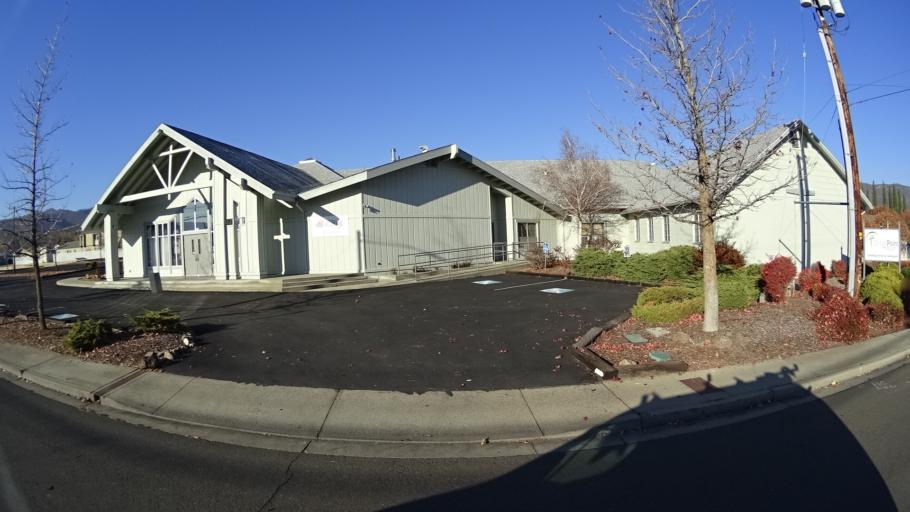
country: US
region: California
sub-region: Siskiyou County
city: Yreka
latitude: 41.7241
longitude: -122.6414
